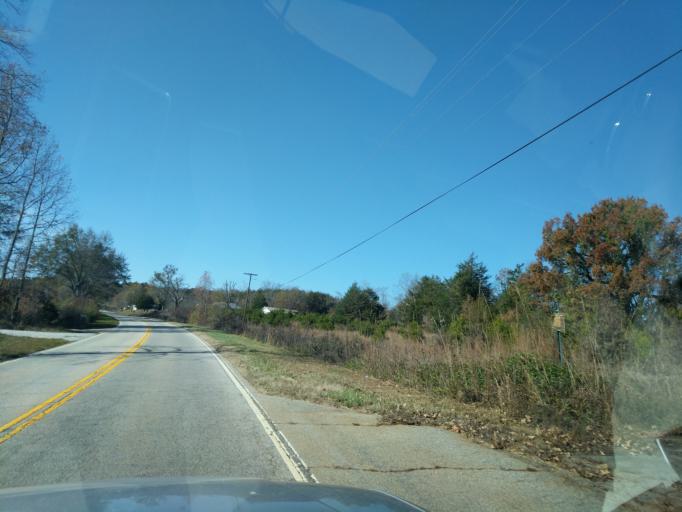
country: US
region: South Carolina
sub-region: Greenville County
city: Tigerville
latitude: 35.0315
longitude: -82.4139
